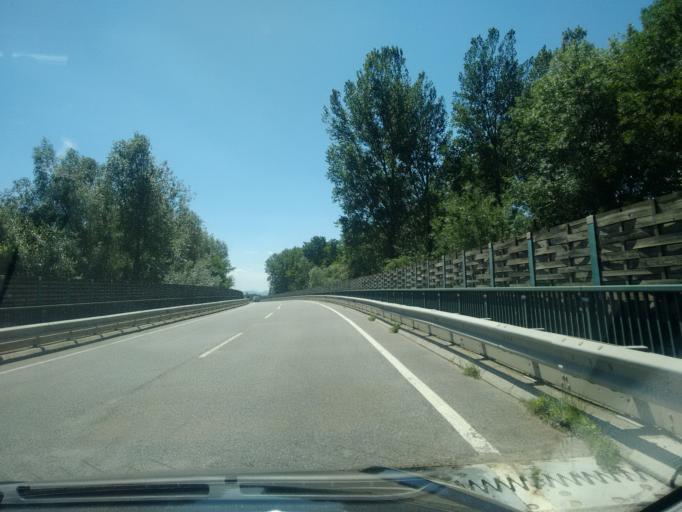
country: AT
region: Lower Austria
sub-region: Politischer Bezirk Sankt Polten
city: Prinzersdorf
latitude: 48.2062
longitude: 15.5046
